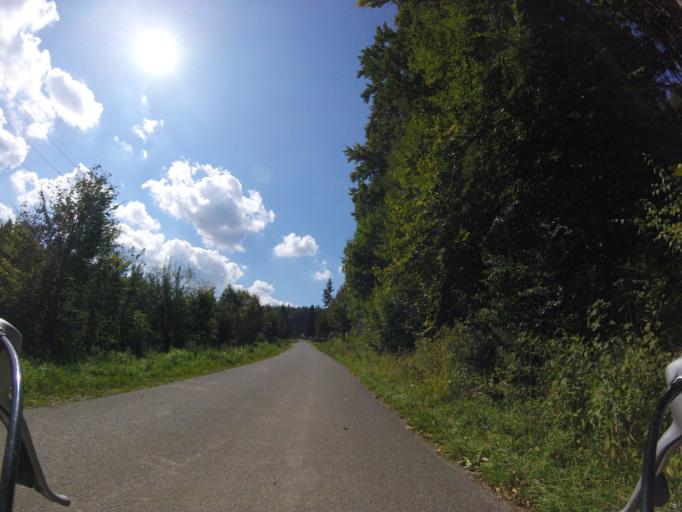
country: HU
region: Heves
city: Szilvasvarad
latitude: 48.0994
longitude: 20.5293
